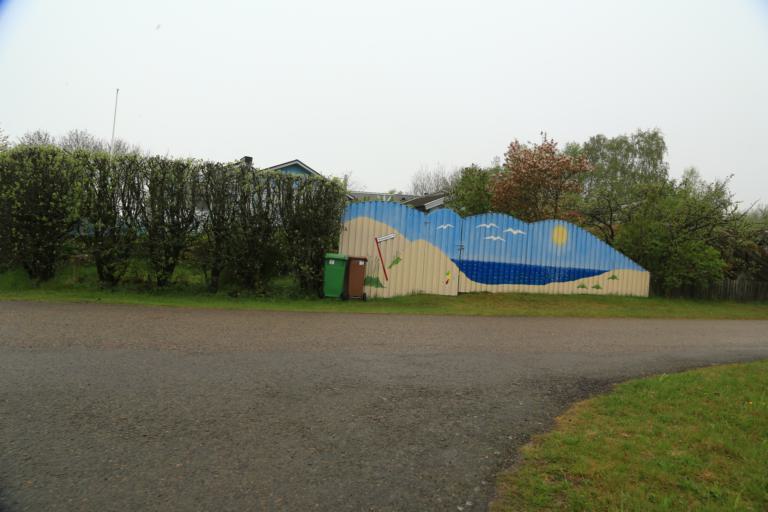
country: SE
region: Halland
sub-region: Varbergs Kommun
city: Varberg
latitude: 57.0874
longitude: 12.2684
